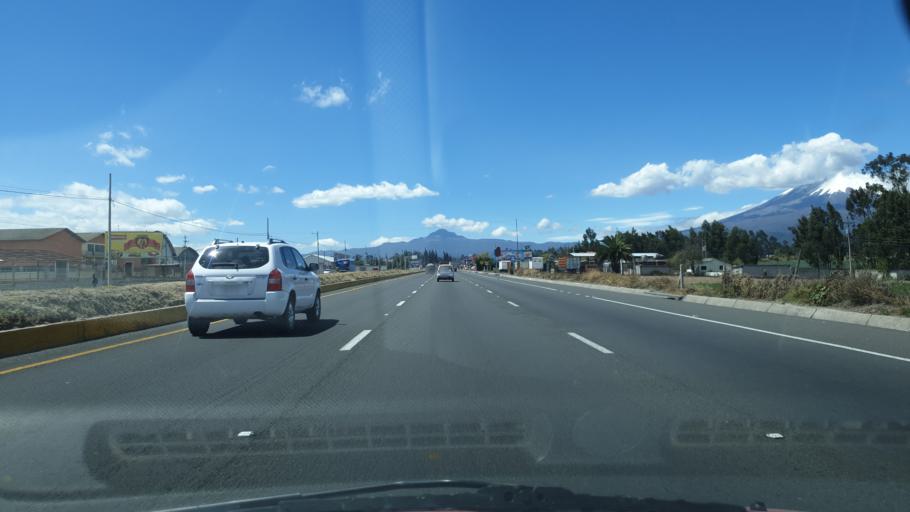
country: EC
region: Cotopaxi
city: Saquisili
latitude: -0.8091
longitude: -78.6235
